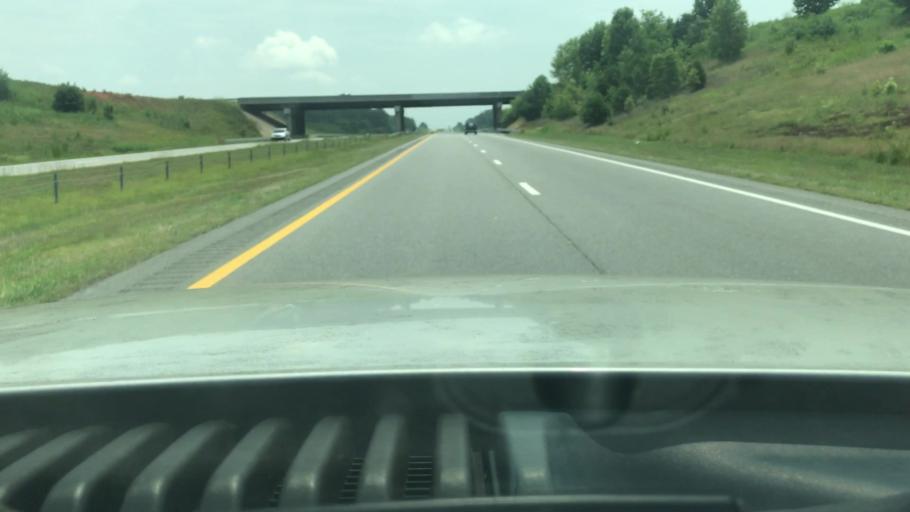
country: US
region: North Carolina
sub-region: Yadkin County
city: Jonesville
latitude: 36.1311
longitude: -80.8441
